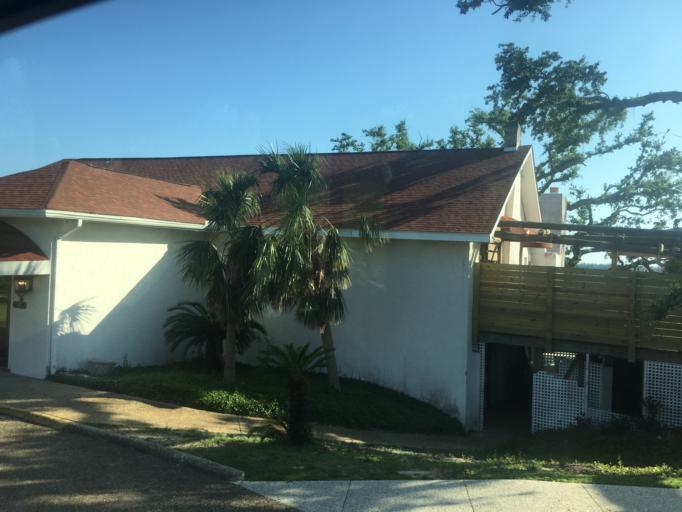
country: US
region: Florida
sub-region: Bay County
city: Panama City
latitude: 30.1433
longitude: -85.6489
